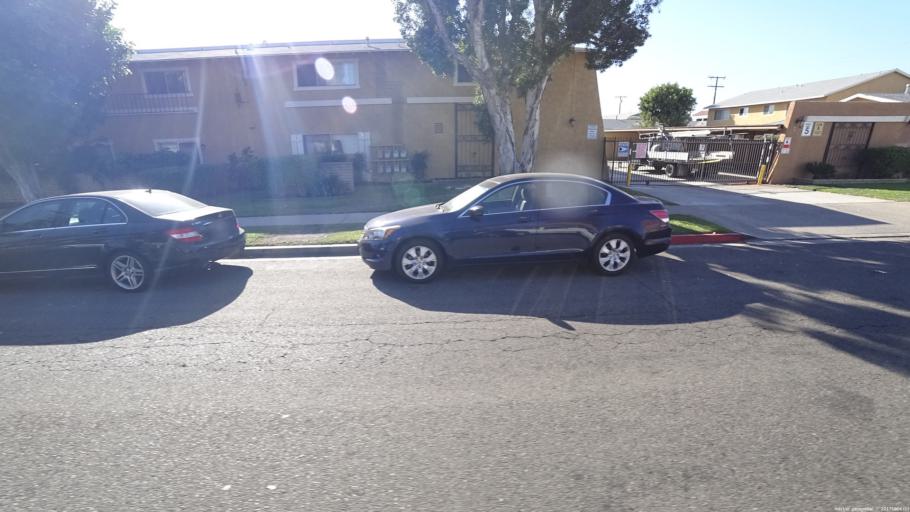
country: US
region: California
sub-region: Orange County
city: Midway City
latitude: 33.7728
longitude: -117.9768
